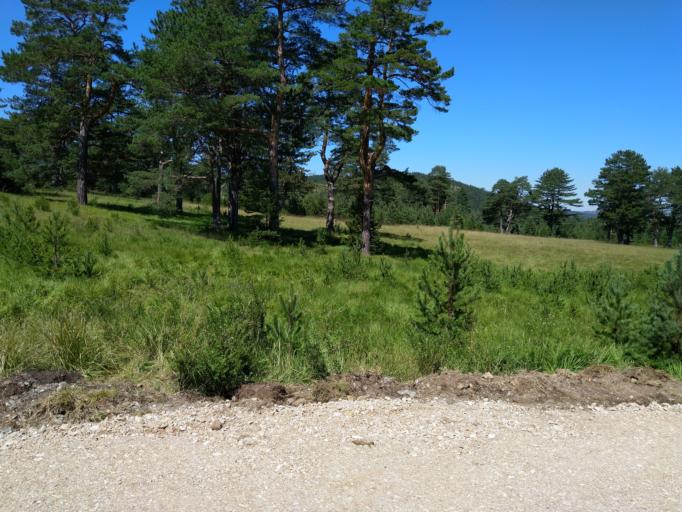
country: RS
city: Zlatibor
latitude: 43.6600
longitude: 19.6896
